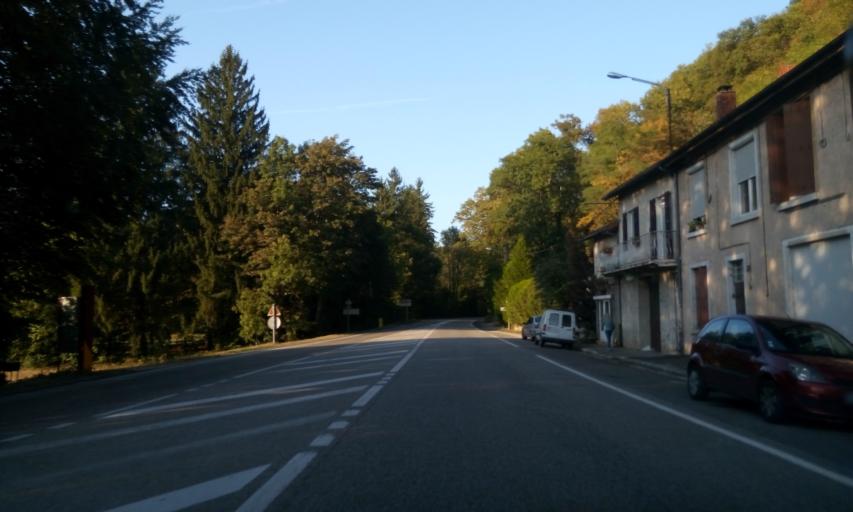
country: FR
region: Rhone-Alpes
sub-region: Departement de l'Ain
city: Neuville-sur-Ain
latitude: 46.0800
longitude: 5.3838
